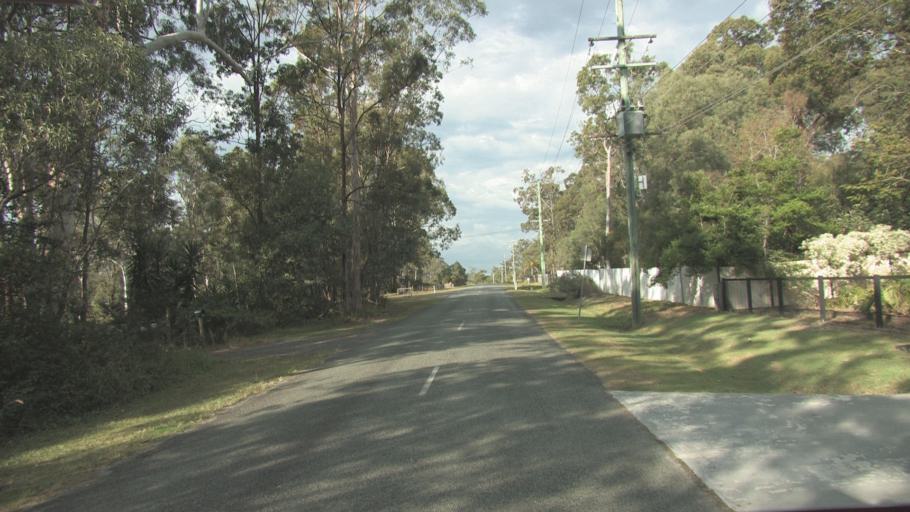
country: AU
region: Queensland
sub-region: Logan
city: Chambers Flat
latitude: -27.7785
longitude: 153.1053
